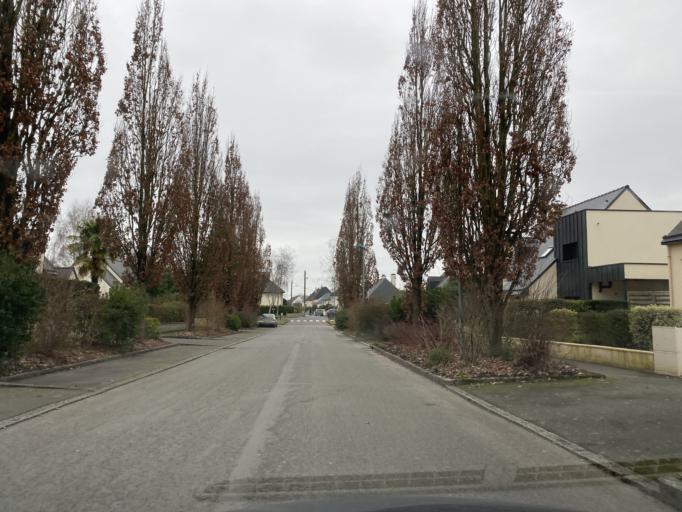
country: FR
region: Brittany
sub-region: Departement d'Ille-et-Vilaine
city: Melesse
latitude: 48.2221
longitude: -1.6956
